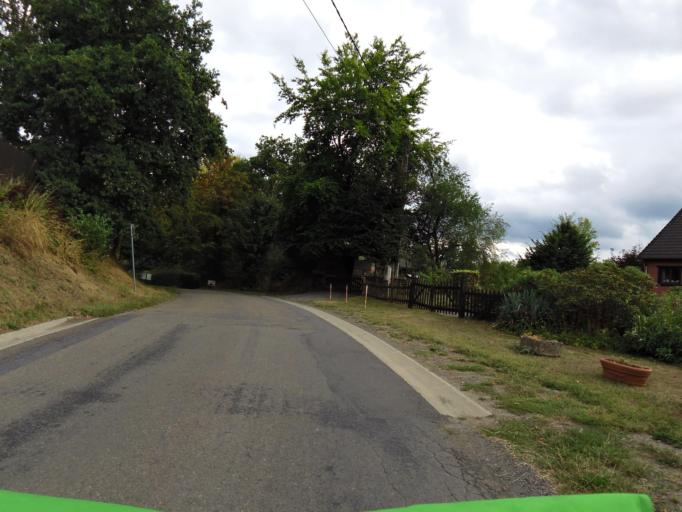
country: BE
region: Wallonia
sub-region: Province de Namur
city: Bievre
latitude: 49.9039
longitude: 4.9908
